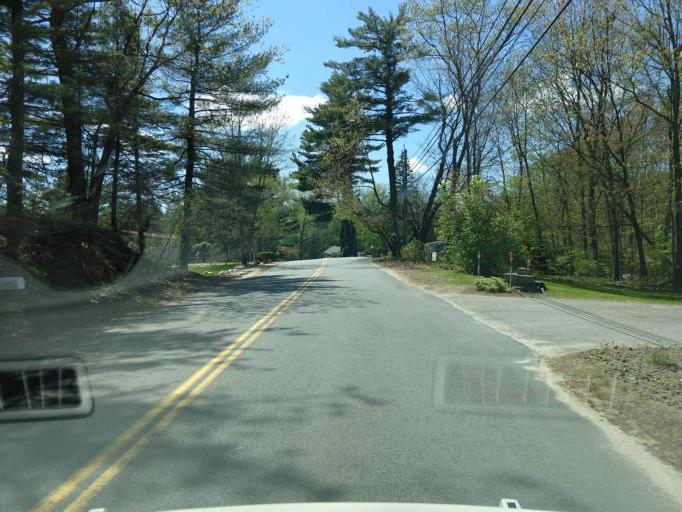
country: US
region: Massachusetts
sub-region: Essex County
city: Amesbury
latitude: 42.8814
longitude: -70.9046
